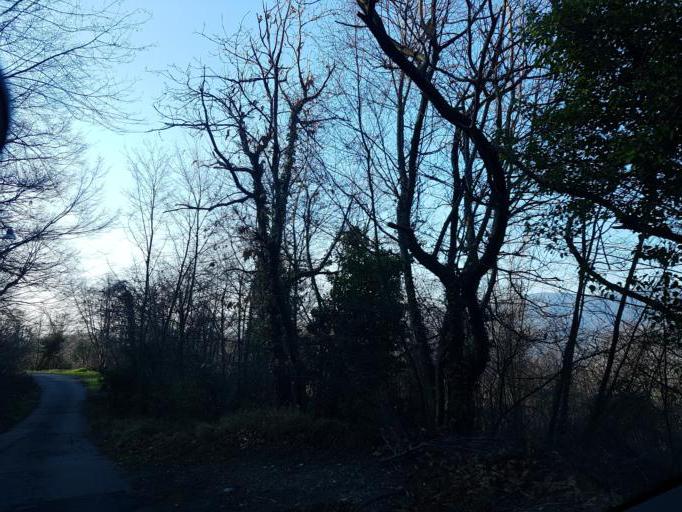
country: IT
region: Liguria
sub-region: Provincia di Genova
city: Manesseno
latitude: 44.4594
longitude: 8.9254
